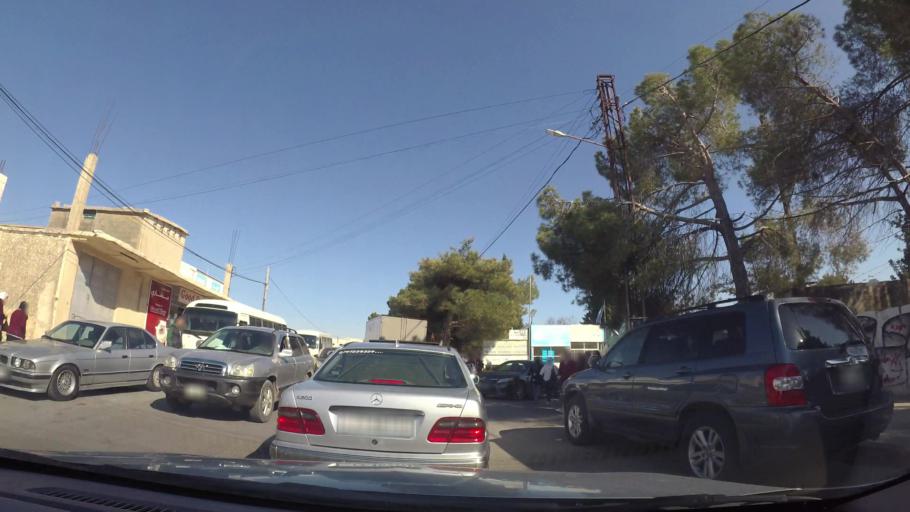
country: JO
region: Amman
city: Al Bunayyat ash Shamaliyah
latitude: 31.9091
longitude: 35.8946
